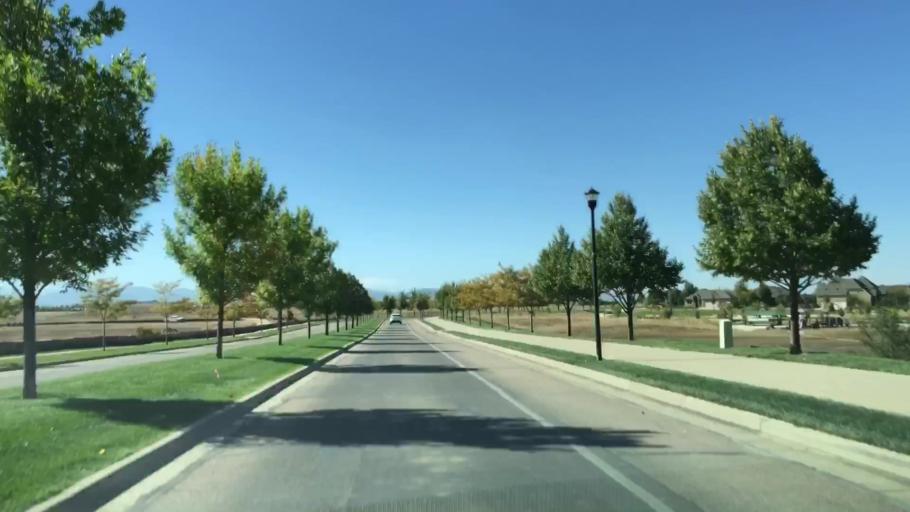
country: US
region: Colorado
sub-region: Weld County
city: Windsor
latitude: 40.4433
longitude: -104.9710
